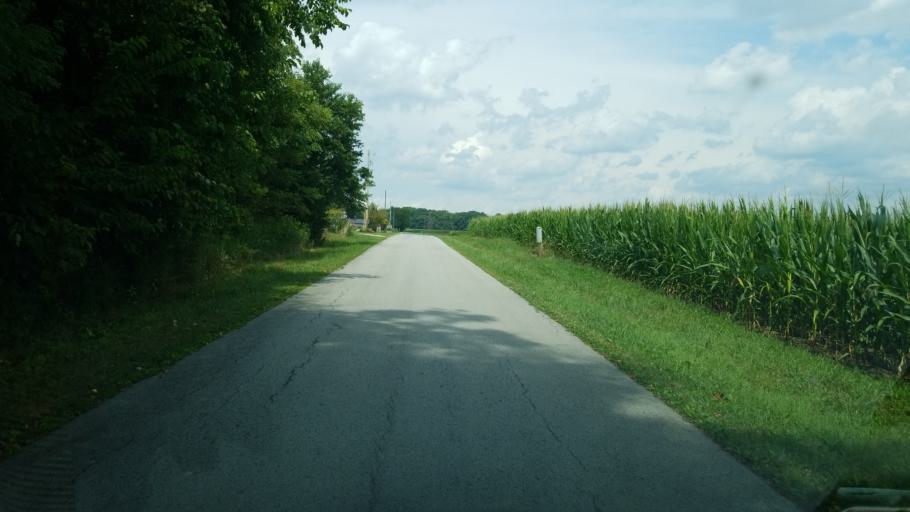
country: US
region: Ohio
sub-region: Hancock County
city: Arlington
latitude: 40.9446
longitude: -83.5425
